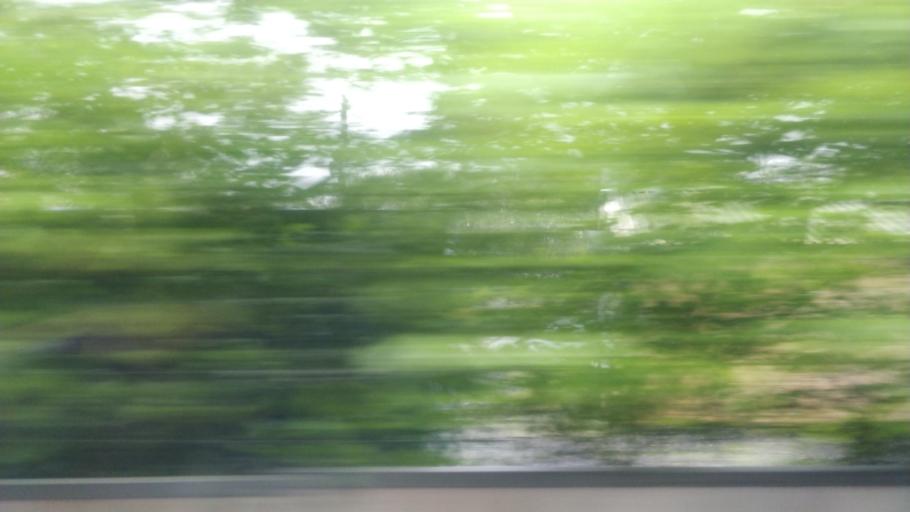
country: GB
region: England
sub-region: Borough of Wigan
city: Shevington
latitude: 53.5592
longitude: -2.6925
